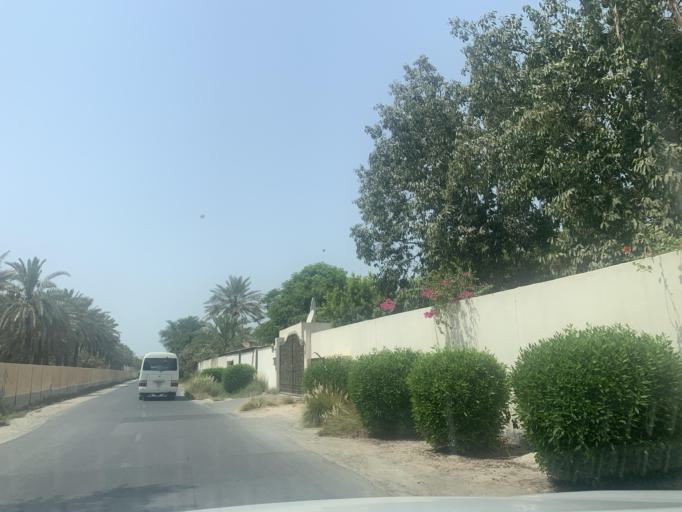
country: BH
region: Manama
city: Jidd Hafs
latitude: 26.2260
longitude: 50.4663
